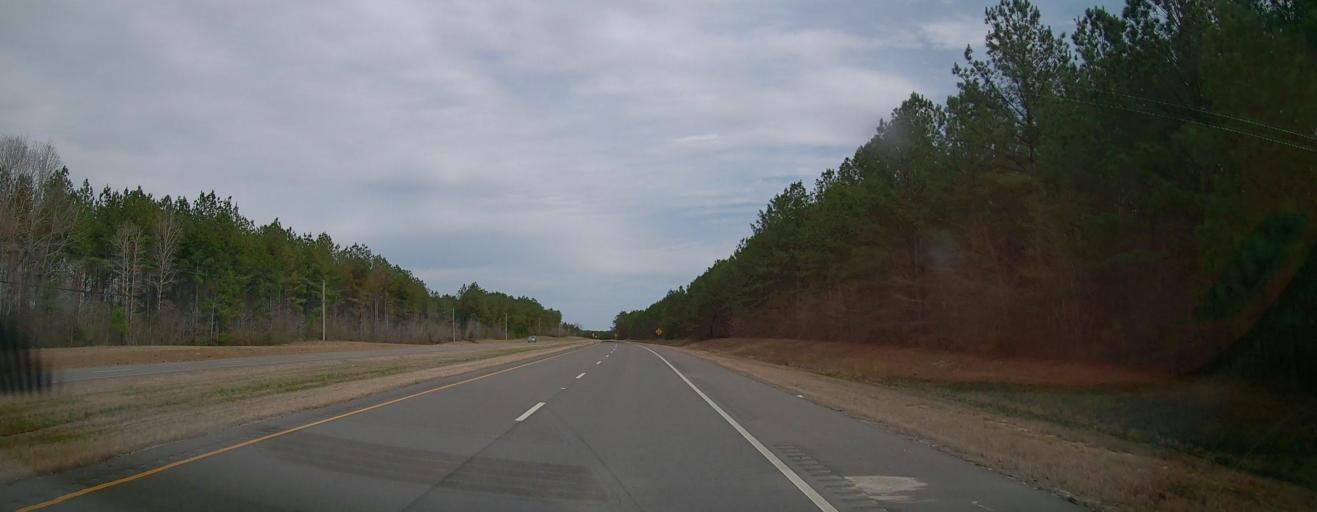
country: US
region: Alabama
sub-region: Walker County
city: Carbon Hill
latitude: 33.8675
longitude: -87.4270
